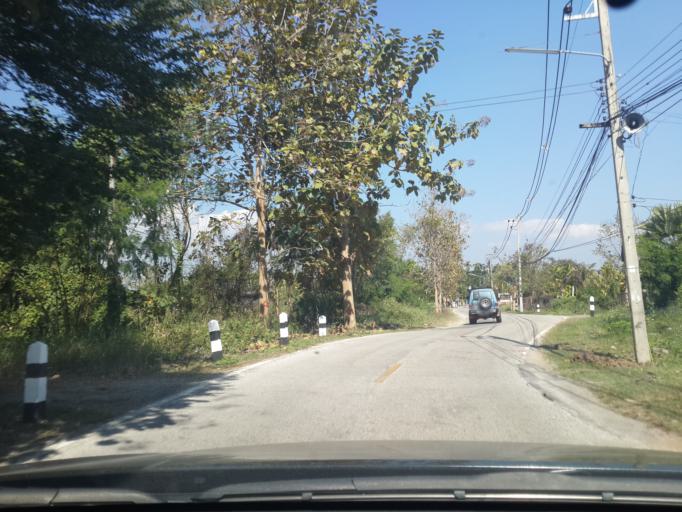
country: TH
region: Chiang Mai
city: San Sai
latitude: 18.8739
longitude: 99.0951
